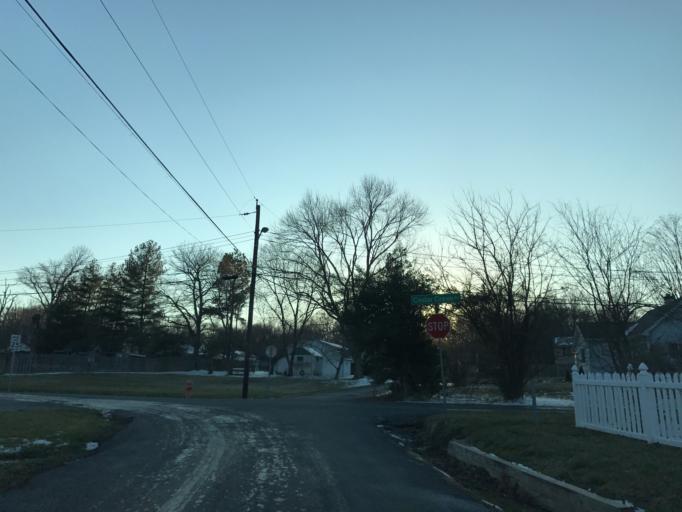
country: US
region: Maryland
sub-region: Baltimore County
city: Edgemere
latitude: 39.2818
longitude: -76.4171
